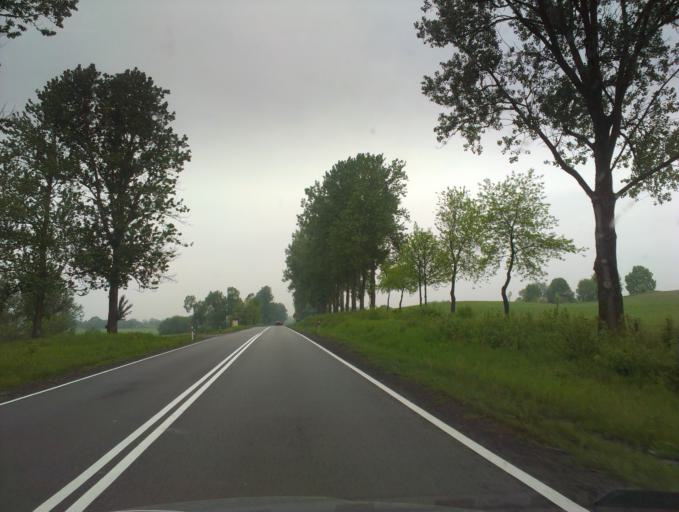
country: PL
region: West Pomeranian Voivodeship
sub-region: Powiat koszalinski
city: Bobolice
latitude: 53.9335
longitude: 16.5968
